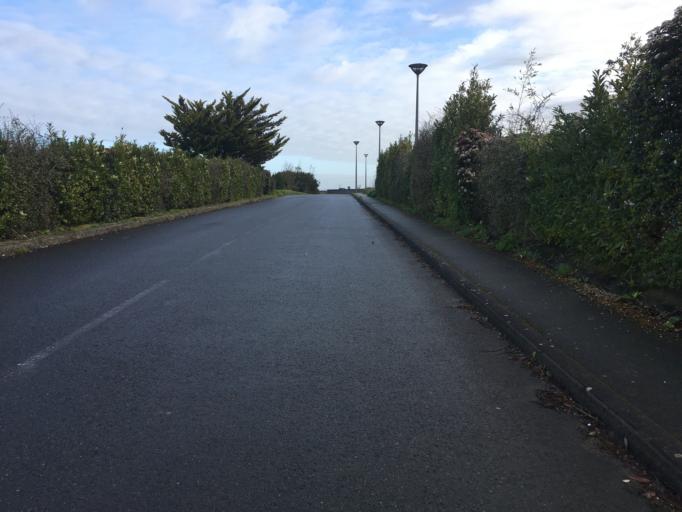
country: FR
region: Poitou-Charentes
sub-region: Departement de la Charente-Maritime
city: Puilboreau
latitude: 46.1748
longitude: -1.1272
